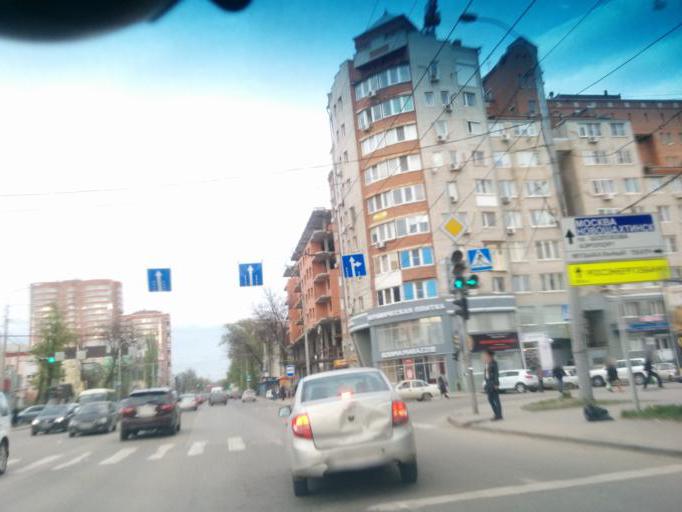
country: RU
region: Rostov
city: Rostov-na-Donu
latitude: 47.2311
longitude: 39.7274
